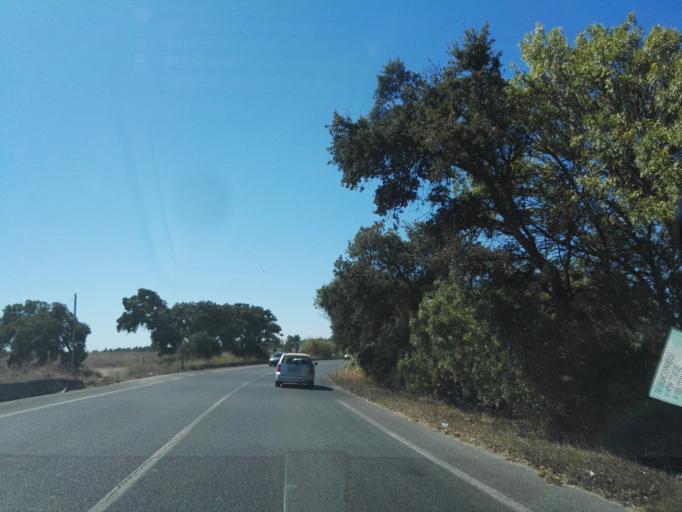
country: PT
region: Santarem
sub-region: Benavente
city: Samora Correia
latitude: 38.9373
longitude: -8.8460
